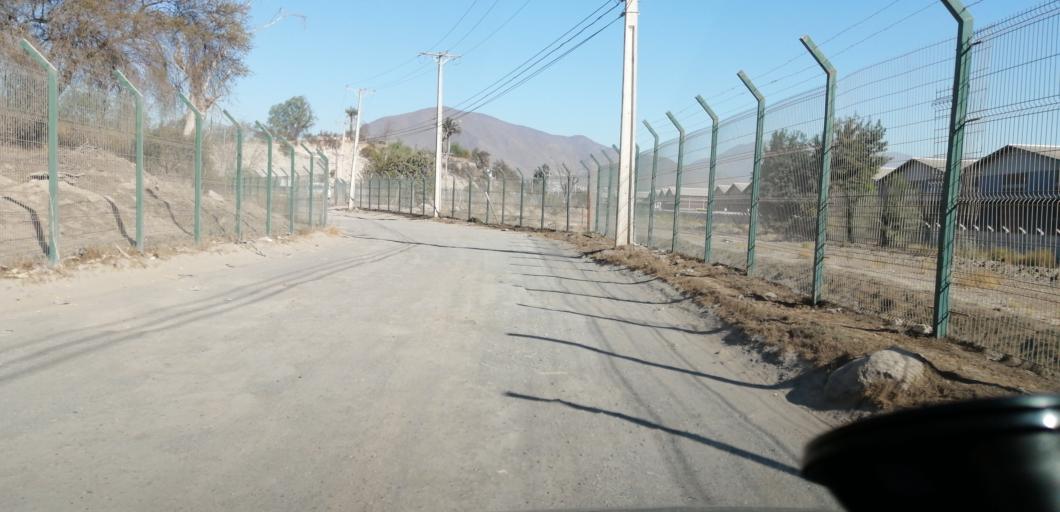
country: CL
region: Santiago Metropolitan
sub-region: Provincia de Santiago
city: Lo Prado
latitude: -33.4629
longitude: -70.7775
